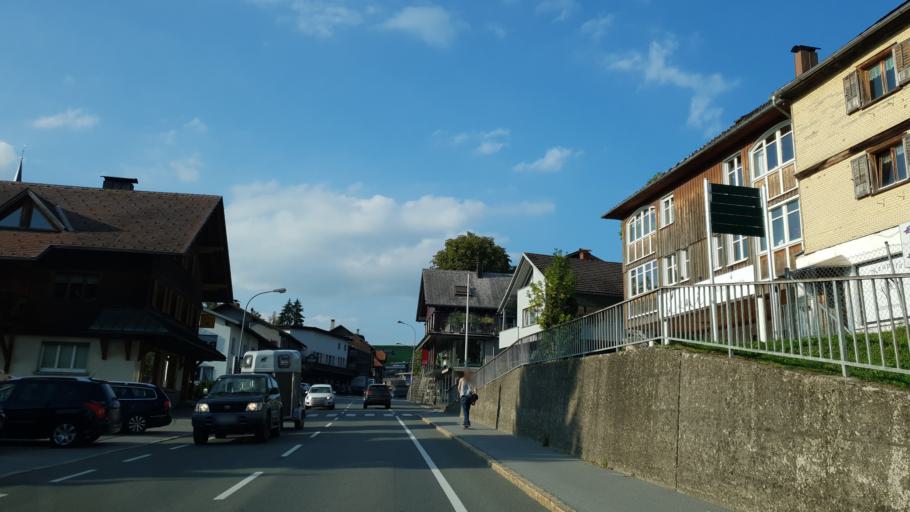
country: AT
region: Vorarlberg
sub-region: Politischer Bezirk Bregenz
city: Egg
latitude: 47.4299
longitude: 9.8973
